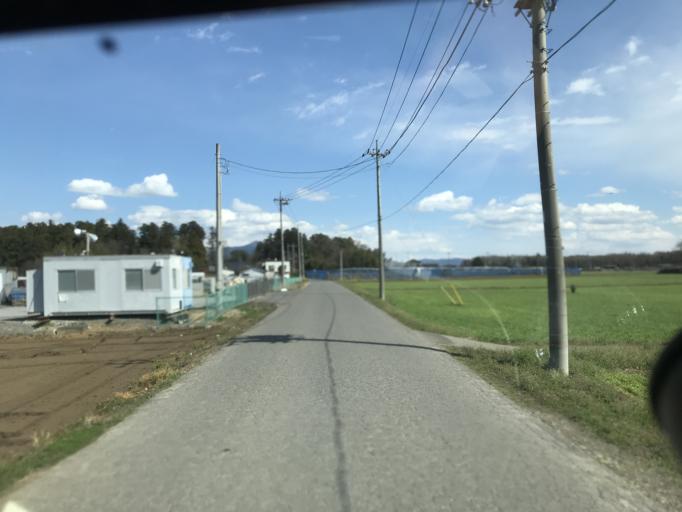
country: JP
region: Ibaraki
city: Shimodate
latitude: 36.2335
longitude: 139.9429
